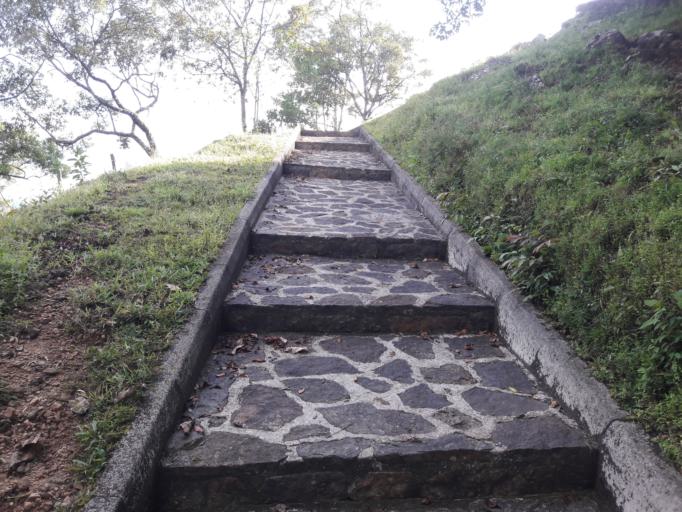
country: CO
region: Casanare
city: Nunchia
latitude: 5.6315
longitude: -72.4243
